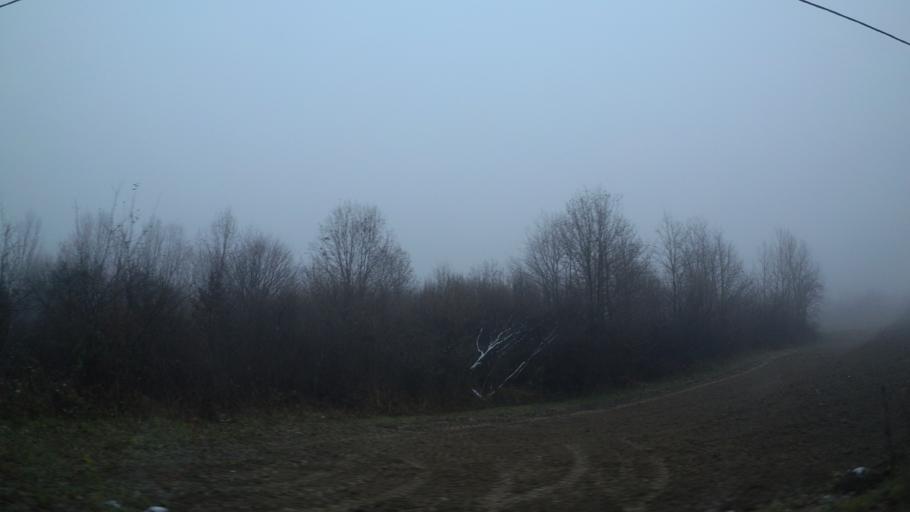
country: HR
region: Sisacko-Moslavacka
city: Glina
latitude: 45.3392
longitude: 16.0429
